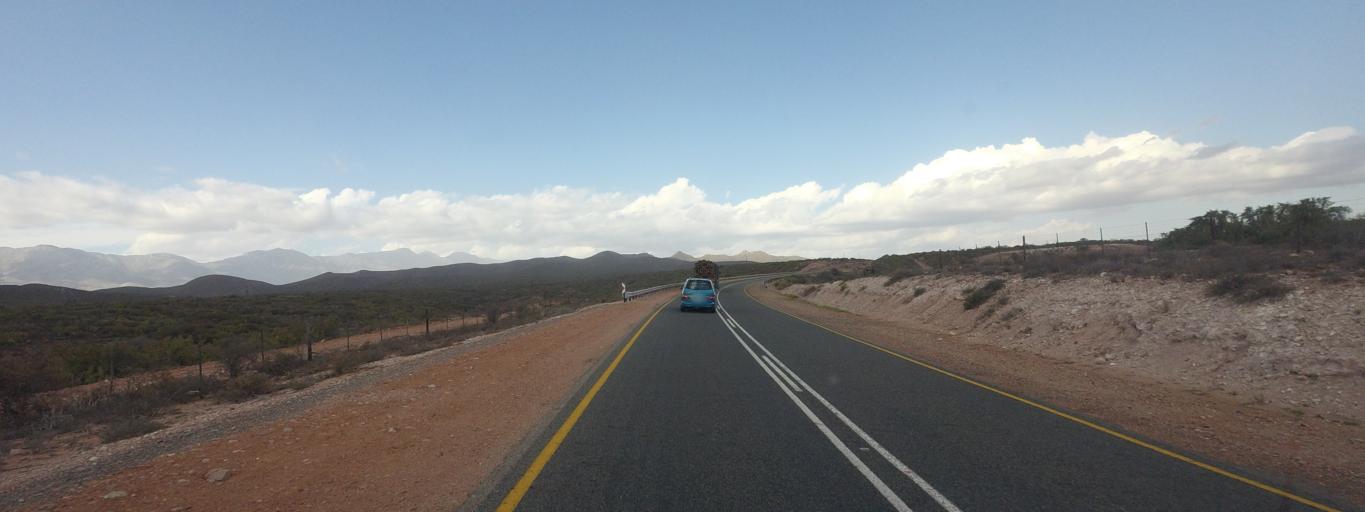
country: ZA
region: Western Cape
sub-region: Central Karoo District Municipality
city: Prince Albert
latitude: -33.5243
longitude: 21.7228
